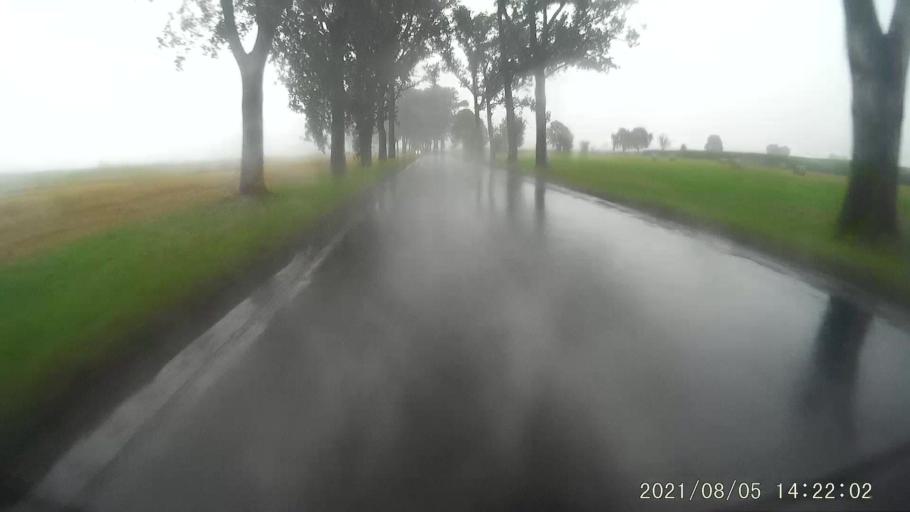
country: PL
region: Opole Voivodeship
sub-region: Powiat nyski
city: Korfantow
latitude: 50.4742
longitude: 17.6627
